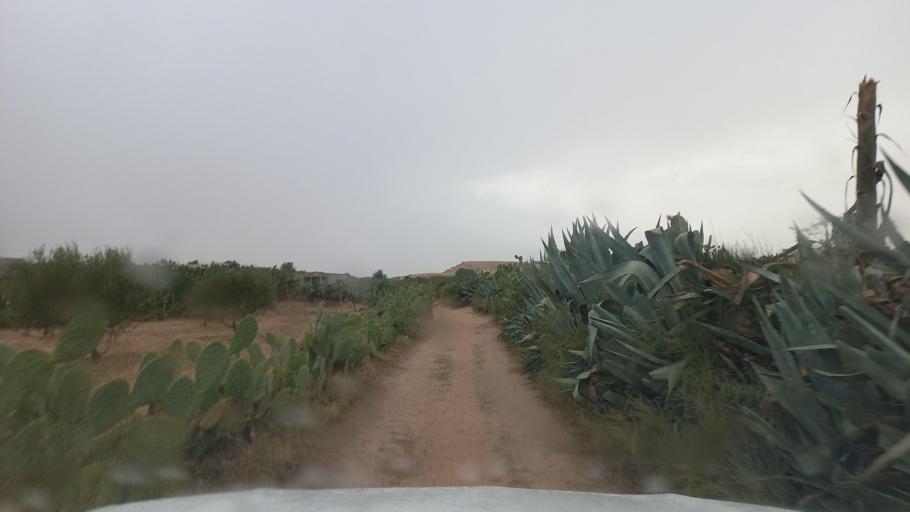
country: TN
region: Al Qasrayn
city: Kasserine
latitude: 35.2748
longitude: 8.9398
